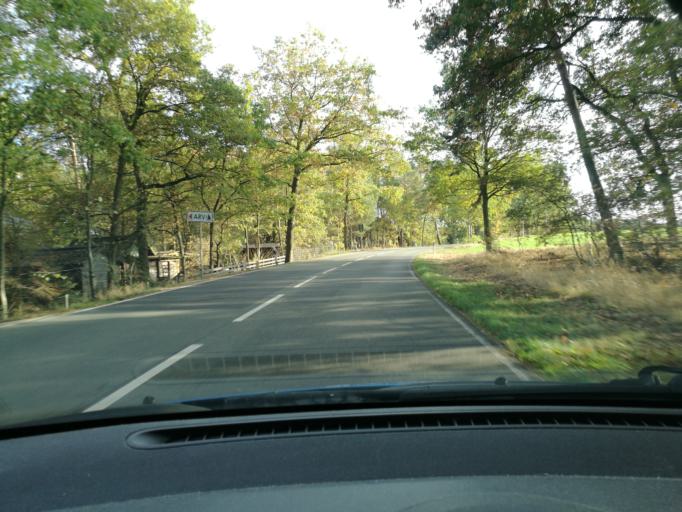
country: DE
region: Saxony-Anhalt
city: Luftkurort Arendsee
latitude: 52.8881
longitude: 11.4494
